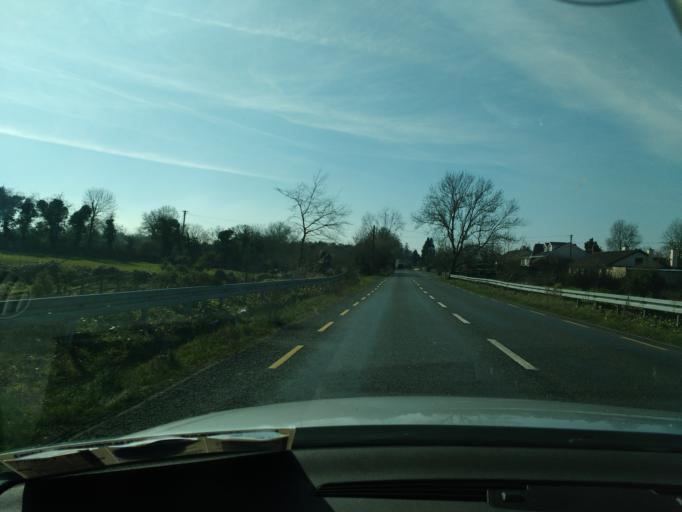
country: IE
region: Munster
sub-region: County Limerick
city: Castleconnell
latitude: 52.6903
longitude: -8.4774
